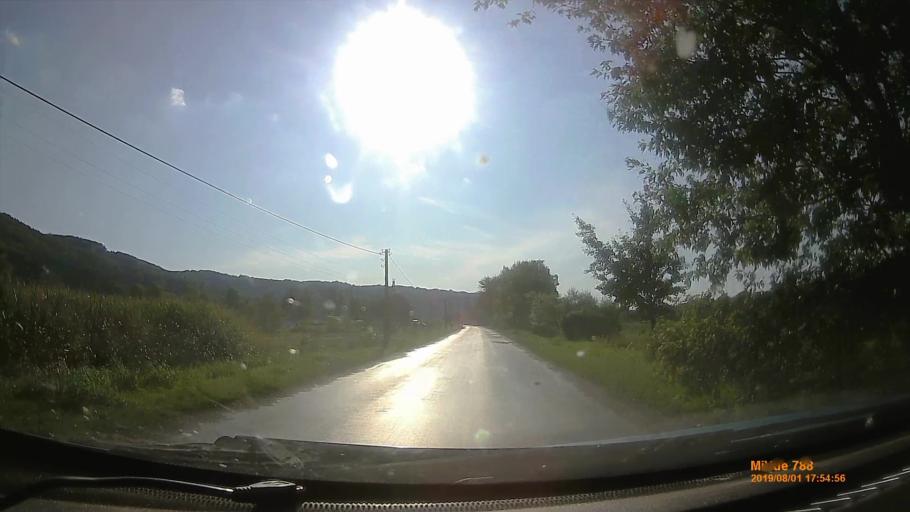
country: HU
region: Baranya
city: Sasd
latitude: 46.1930
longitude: 18.1439
